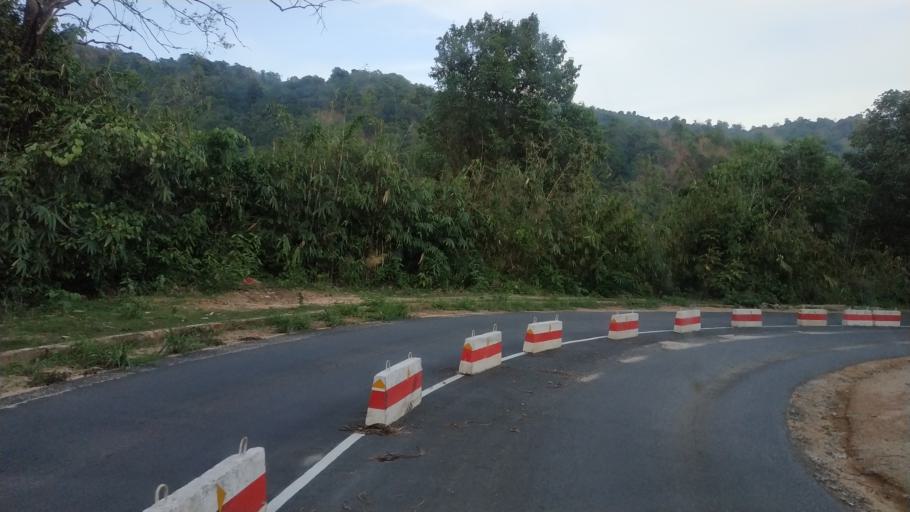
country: MM
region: Mon
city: Kyaikto
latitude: 17.4424
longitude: 97.0980
